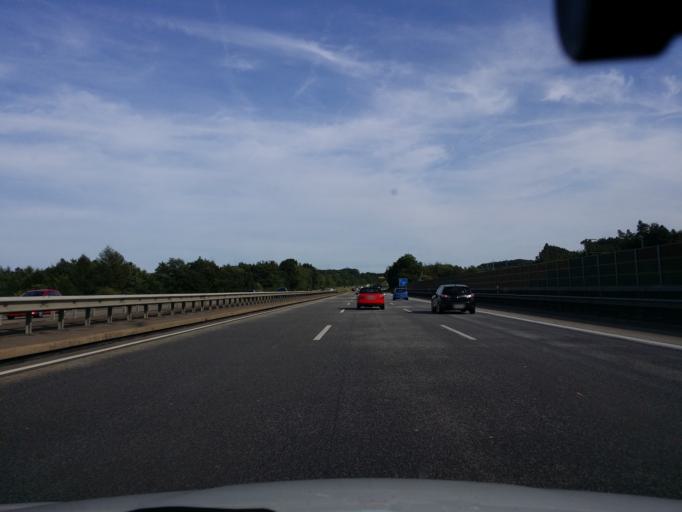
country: DE
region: Rheinland-Pfalz
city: Rossbach
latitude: 50.6176
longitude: 7.4124
